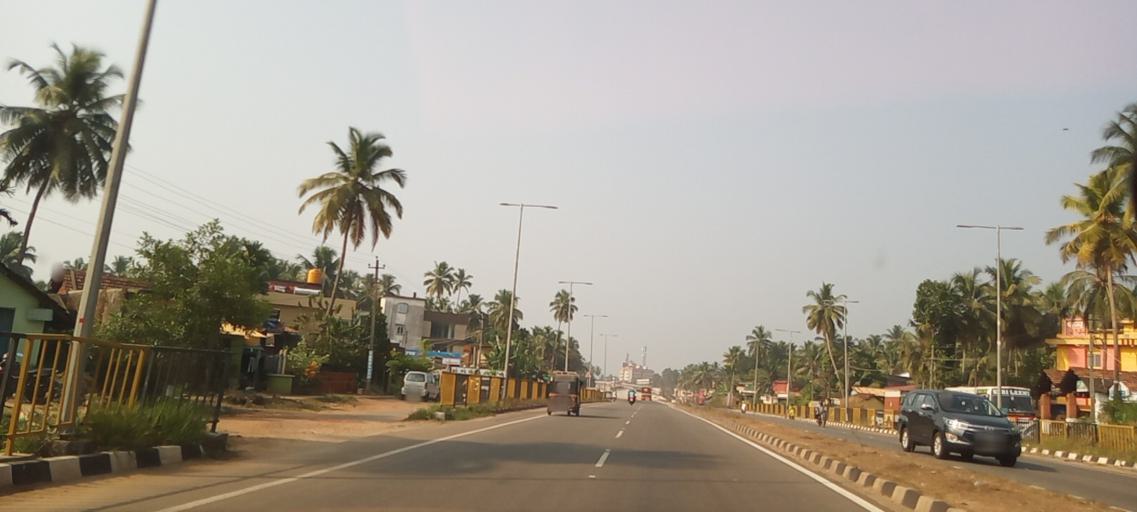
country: IN
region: Karnataka
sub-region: Udupi
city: Coondapoor
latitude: 13.6297
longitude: 74.6976
